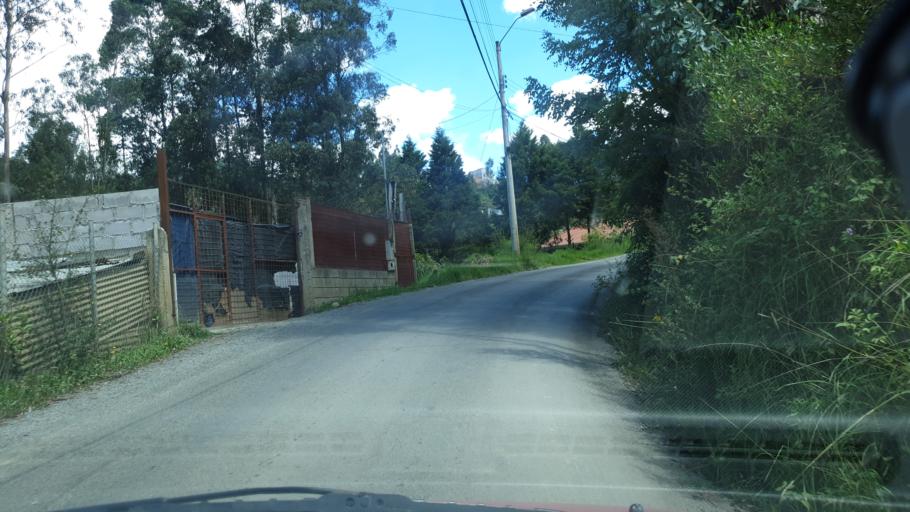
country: EC
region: Azuay
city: Cuenca
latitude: -2.8764
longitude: -78.9509
